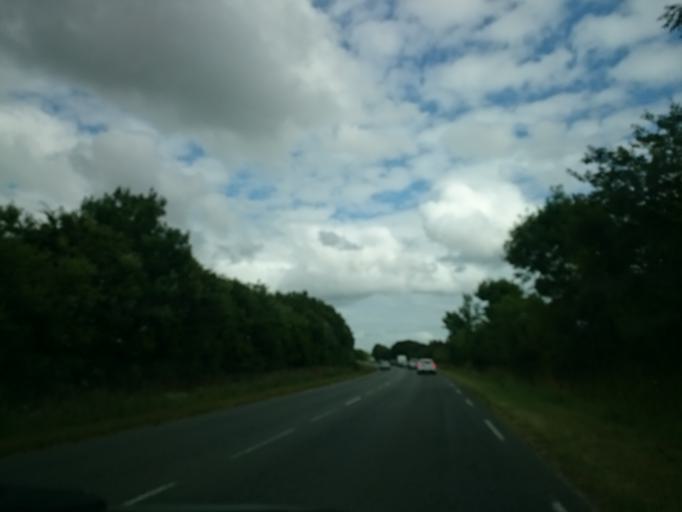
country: FR
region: Brittany
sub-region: Departement du Finistere
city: Gouesnou
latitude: 48.4377
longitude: -4.4524
